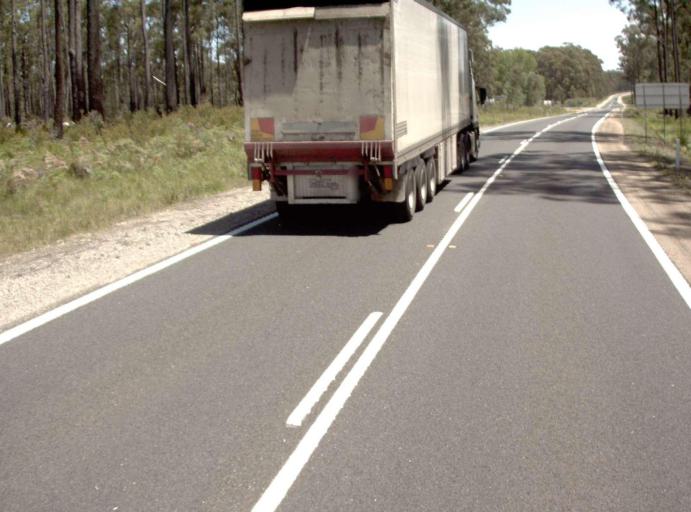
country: AU
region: Victoria
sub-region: East Gippsland
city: Lakes Entrance
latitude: -37.6702
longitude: 148.7976
